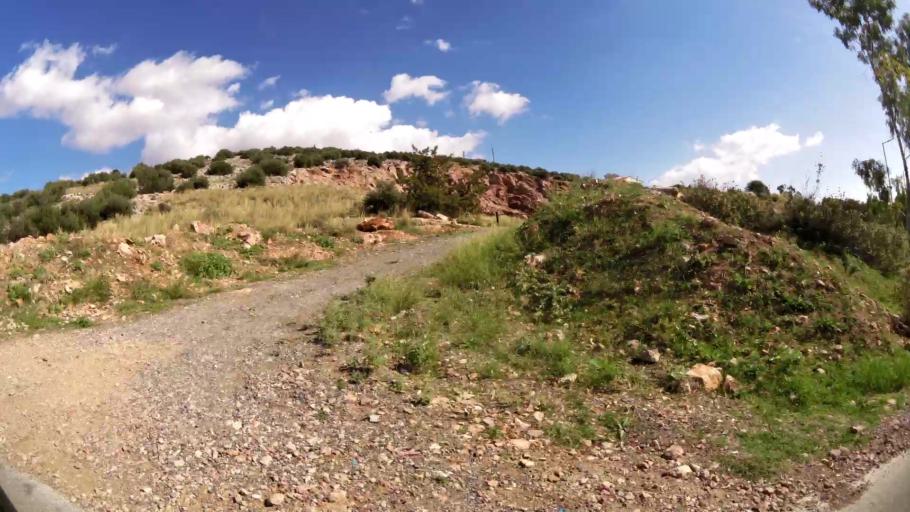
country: GR
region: Attica
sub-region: Nomarchia Anatolikis Attikis
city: Vari
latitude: 37.8366
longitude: 23.7953
